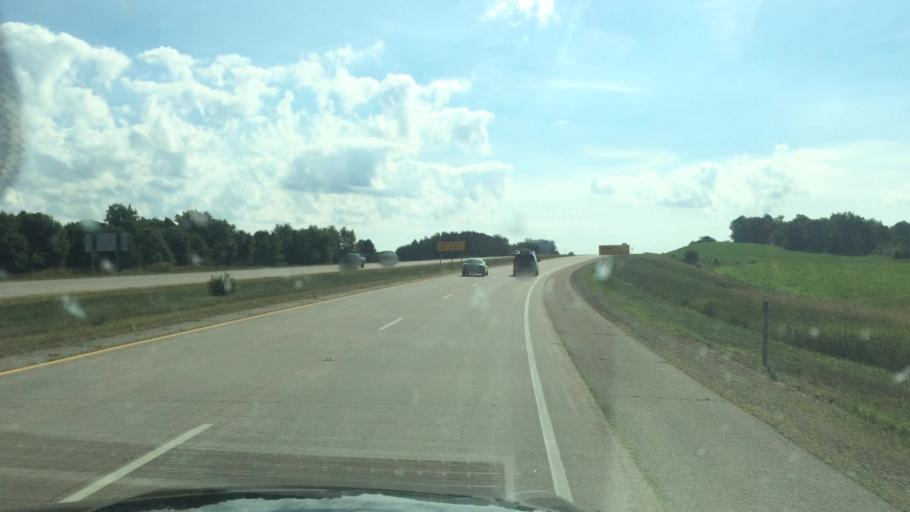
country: US
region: Wisconsin
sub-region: Shawano County
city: Wittenberg
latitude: 44.8258
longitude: -89.1125
